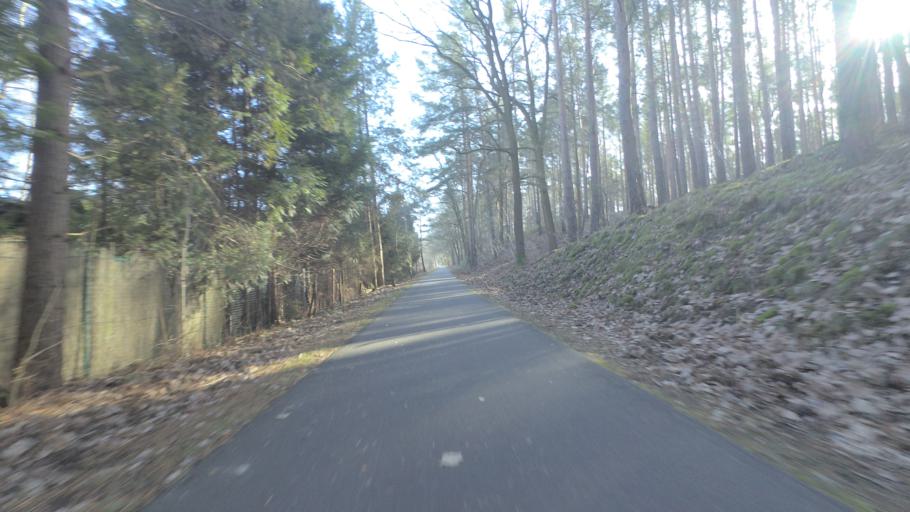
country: DE
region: Brandenburg
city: Luckenwalde
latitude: 52.0734
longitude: 13.1654
